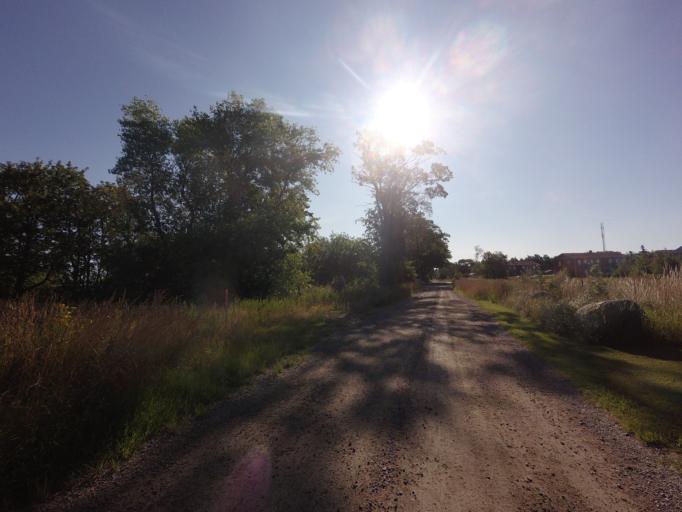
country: SE
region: Skane
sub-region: Hoganas Kommun
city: Hoganas
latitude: 56.1564
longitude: 12.5825
